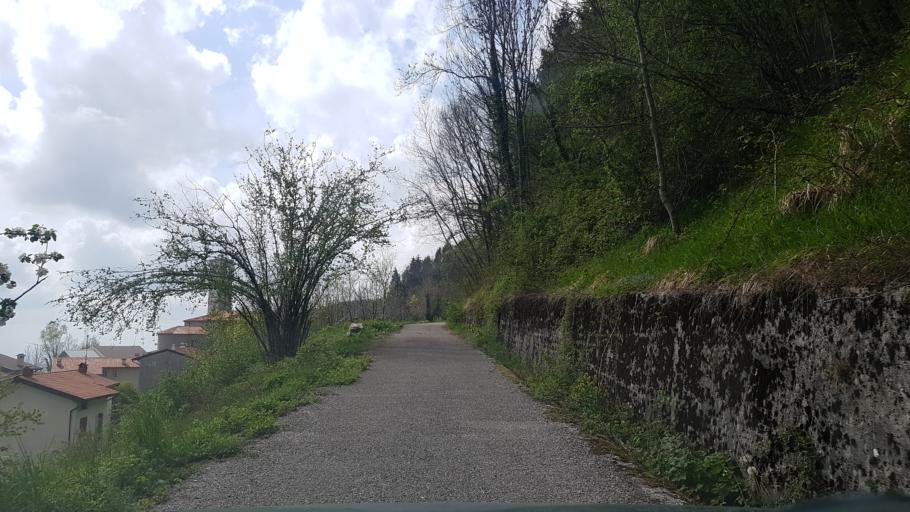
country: IT
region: Friuli Venezia Giulia
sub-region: Provincia di Udine
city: Attimis
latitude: 46.2070
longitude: 13.3469
